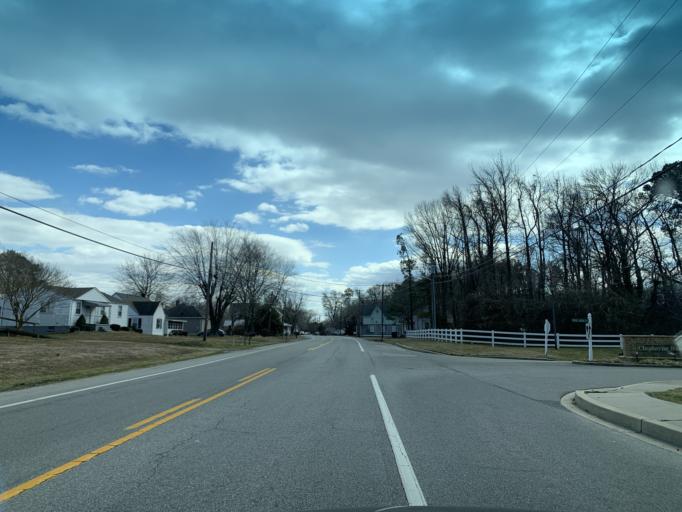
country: US
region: Maryland
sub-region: Queen Anne's County
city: Chester
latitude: 38.9718
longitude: -76.2797
